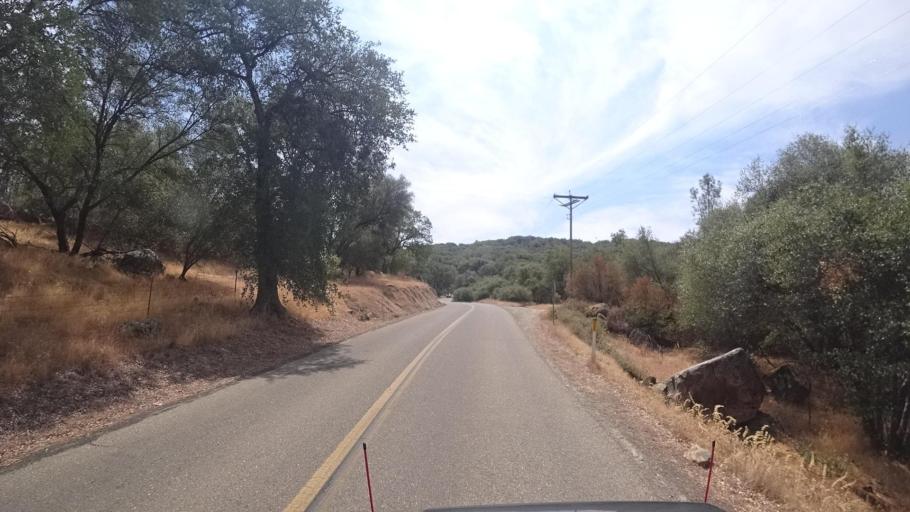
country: US
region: California
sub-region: Mariposa County
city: Mariposa
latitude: 37.4092
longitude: -119.8559
